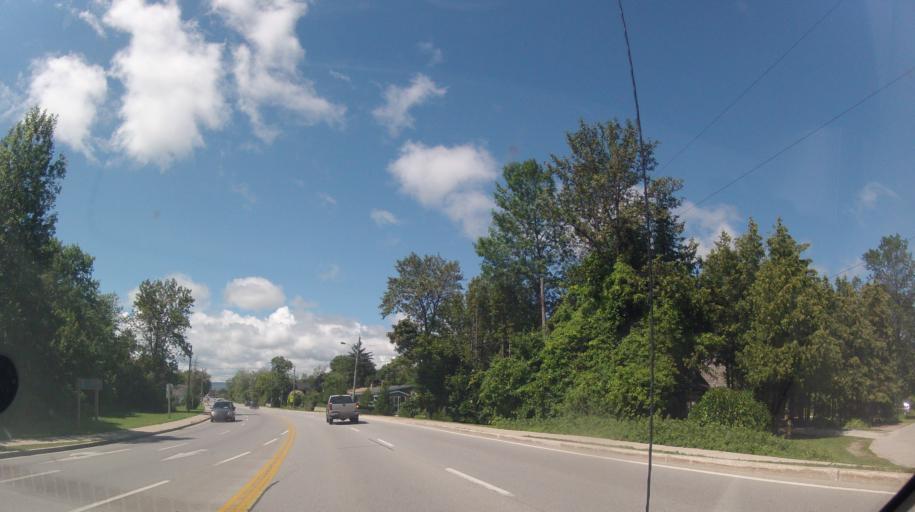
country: CA
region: Ontario
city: Collingwood
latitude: 44.5067
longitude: -80.2063
